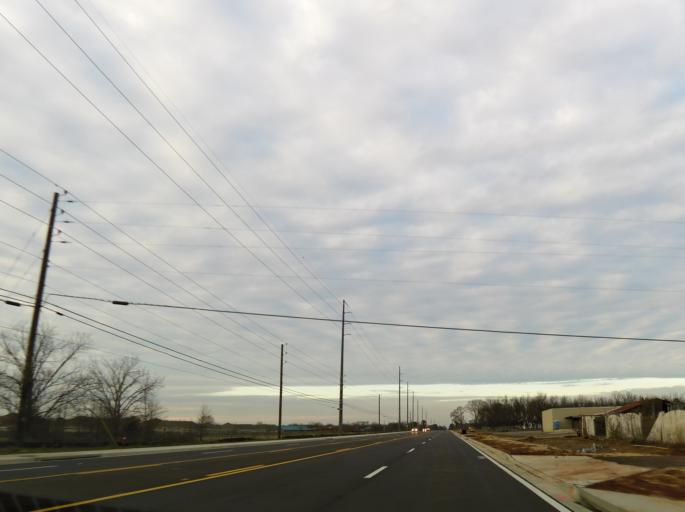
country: US
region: Georgia
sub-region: Houston County
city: Centerville
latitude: 32.6268
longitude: -83.7096
